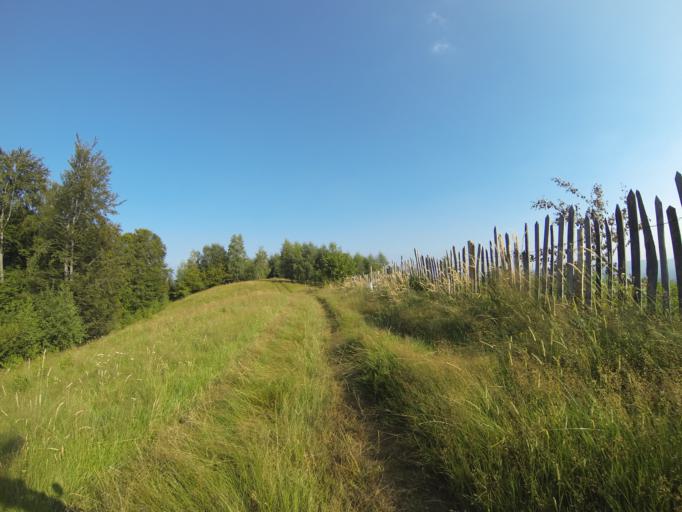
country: RO
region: Valcea
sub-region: Comuna Vaideeni
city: Vaideeni
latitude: 45.2051
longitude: 23.9753
